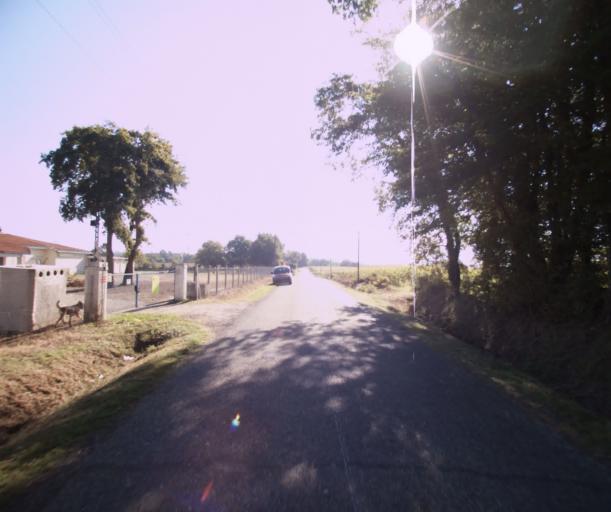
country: FR
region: Aquitaine
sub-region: Departement des Landes
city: Gabarret
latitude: 43.9545
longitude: -0.0149
